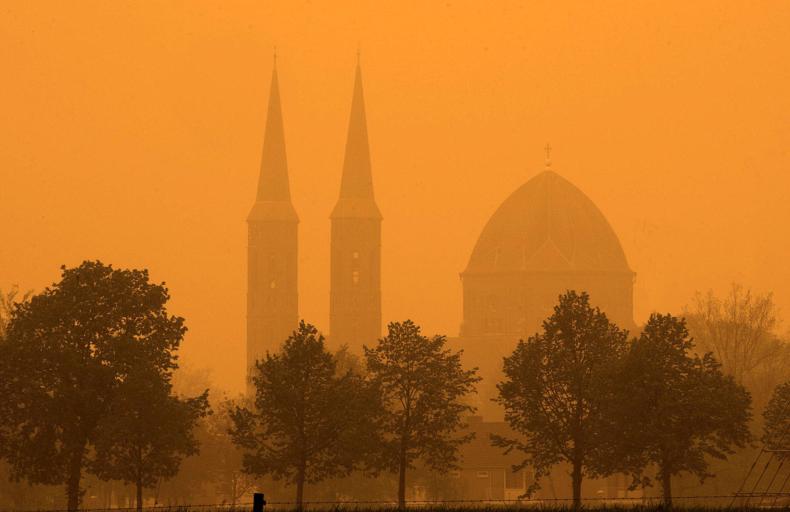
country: NL
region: North Brabant
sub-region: Gemeente Uden
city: Uden
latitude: 51.6629
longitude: 5.5992
